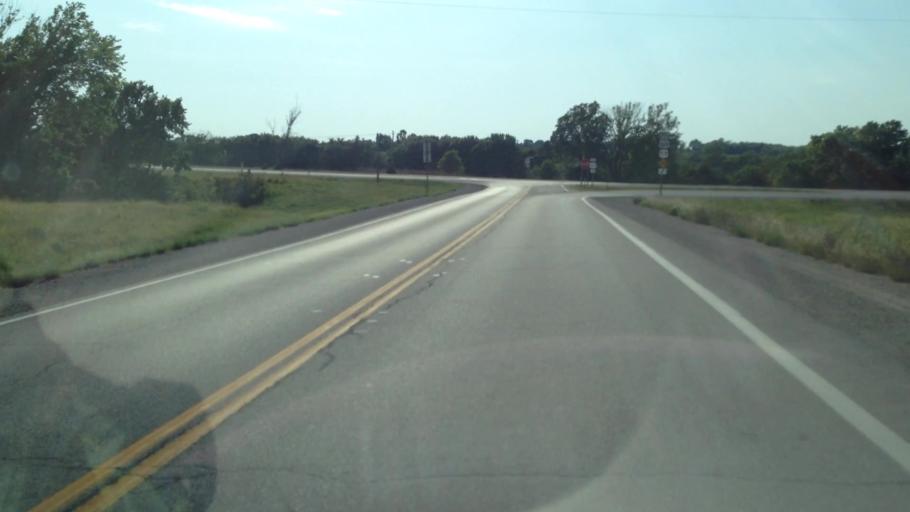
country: US
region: Kansas
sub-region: Anderson County
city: Garnett
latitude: 38.1970
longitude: -95.2492
